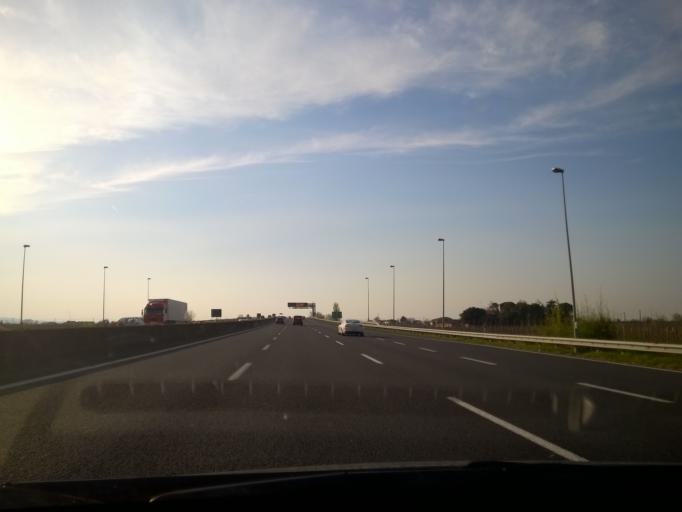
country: IT
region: Emilia-Romagna
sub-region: Provincia di Ravenna
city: Solarolo
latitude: 44.3443
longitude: 11.8436
